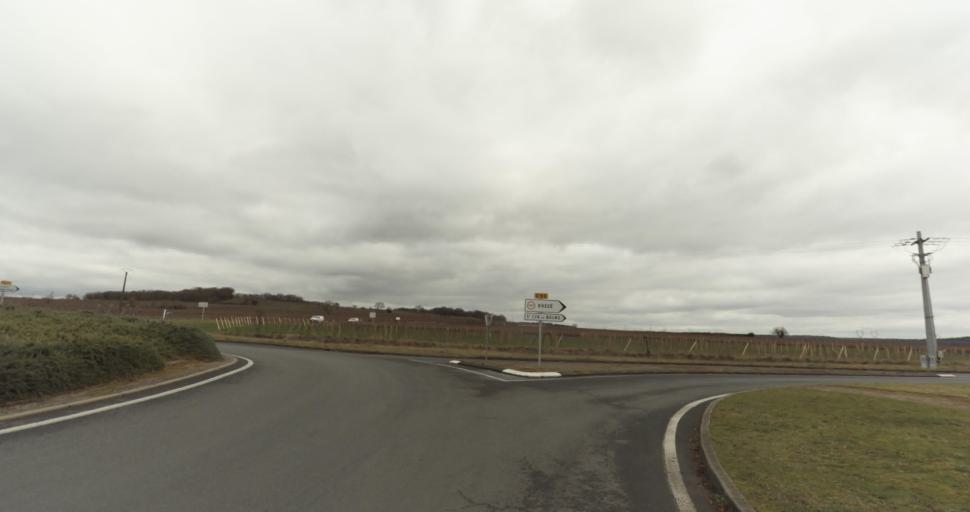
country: FR
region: Pays de la Loire
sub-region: Departement de Maine-et-Loire
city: Varrains
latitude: 47.2137
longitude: -0.0594
